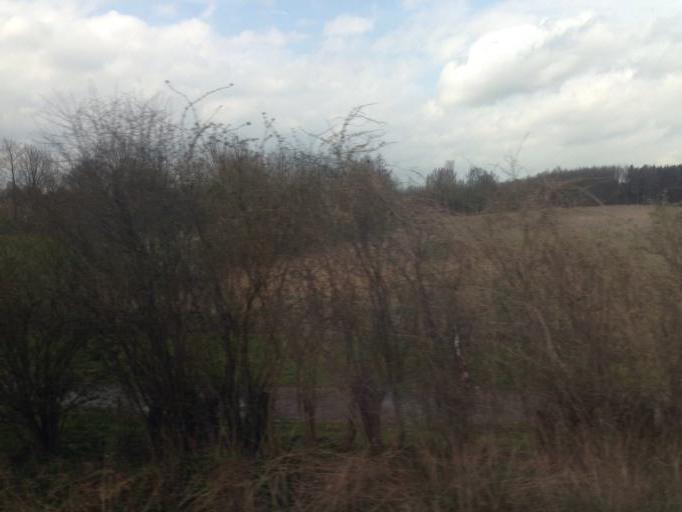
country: DE
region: North Rhine-Westphalia
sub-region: Regierungsbezirk Munster
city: Senden
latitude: 51.8954
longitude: 7.4350
